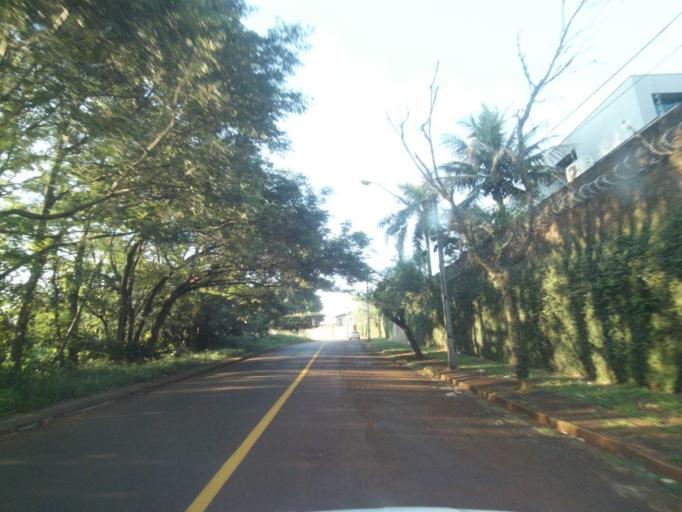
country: BR
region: Parana
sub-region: Londrina
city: Londrina
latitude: -23.3479
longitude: -51.1947
